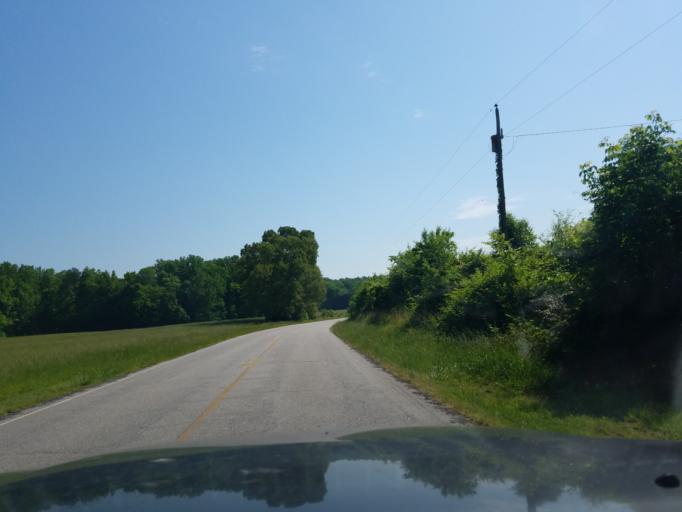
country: US
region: North Carolina
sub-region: Vance County
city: Henderson
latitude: 36.4055
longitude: -78.4119
